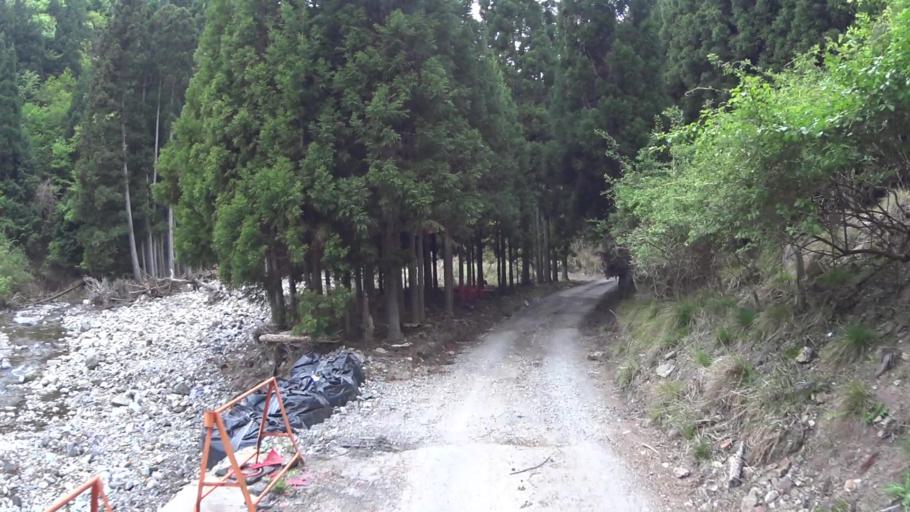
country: JP
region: Kyoto
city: Kameoka
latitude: 35.1169
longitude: 135.6305
